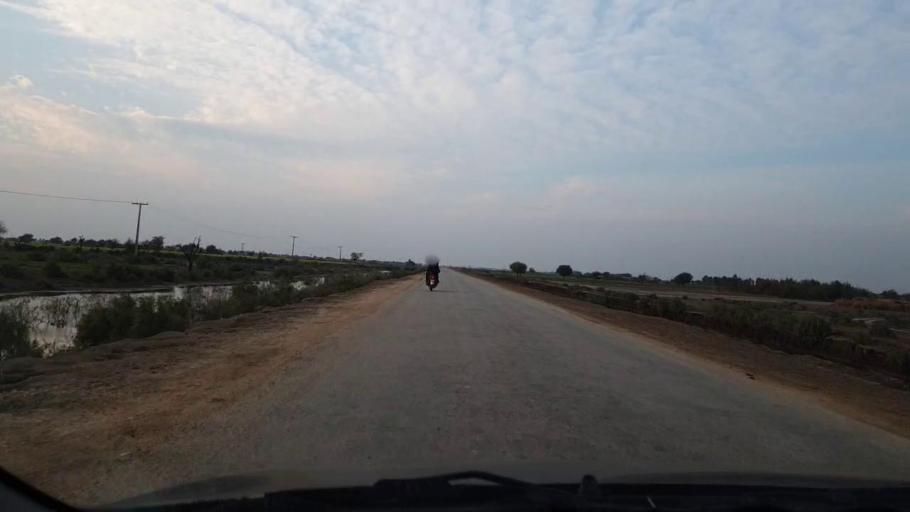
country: PK
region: Sindh
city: Jhol
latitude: 25.9951
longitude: 68.8517
